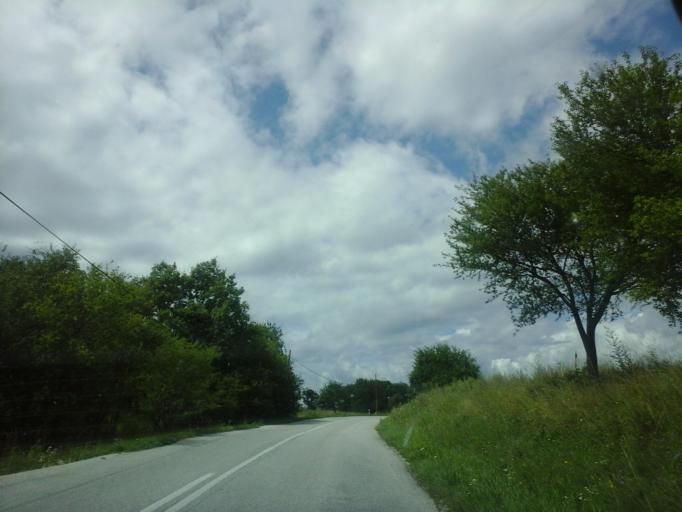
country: HU
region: Borsod-Abauj-Zemplen
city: Putnok
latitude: 48.4778
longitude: 20.4646
